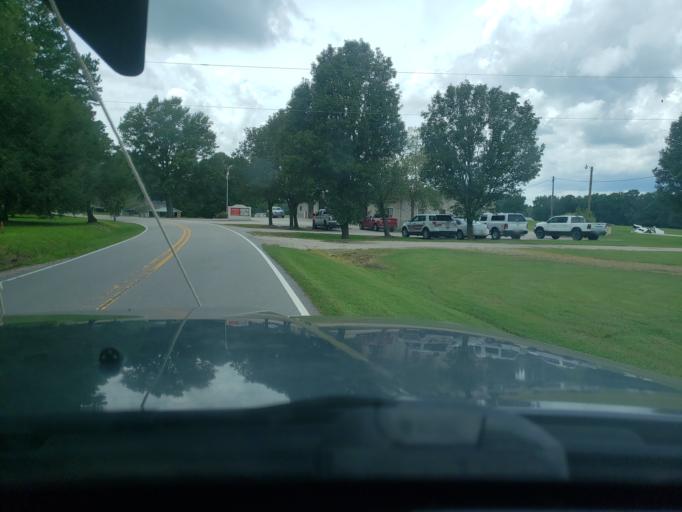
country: US
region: North Carolina
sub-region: Wake County
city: Zebulon
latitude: 35.8849
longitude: -78.3538
